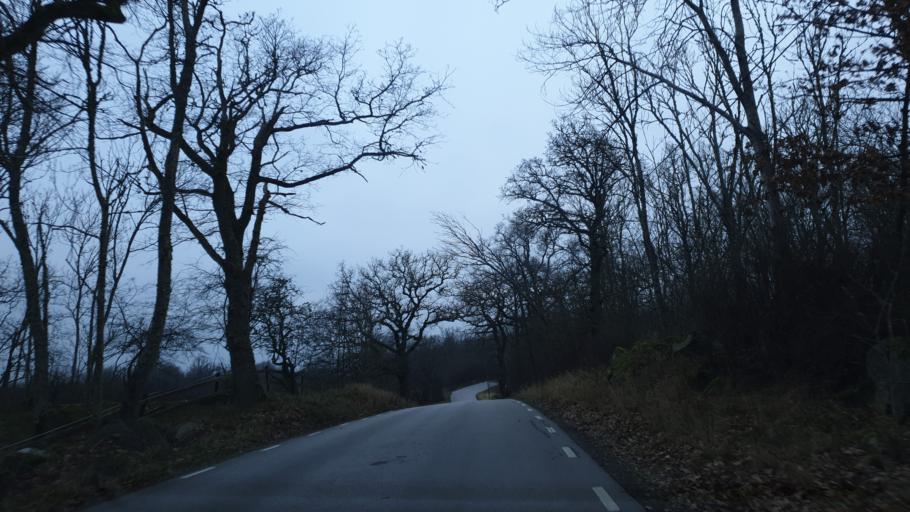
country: SE
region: Blekinge
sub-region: Karlskrona Kommun
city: Rodeby
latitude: 56.2010
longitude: 15.6873
